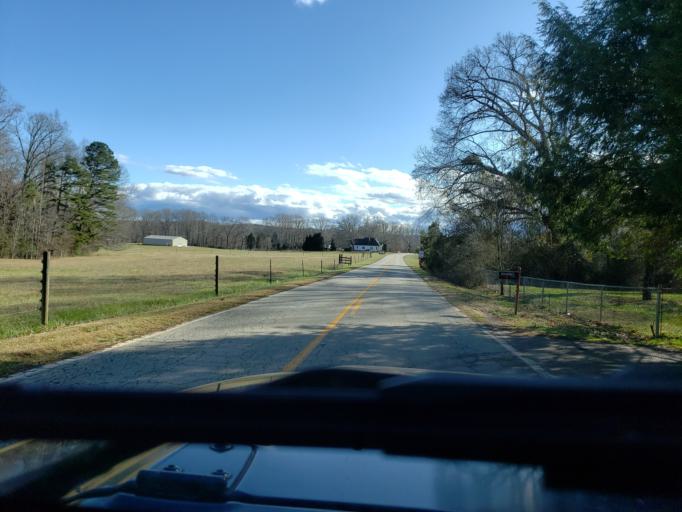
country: US
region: North Carolina
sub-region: Cleveland County
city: White Plains
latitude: 35.1670
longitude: -81.4069
